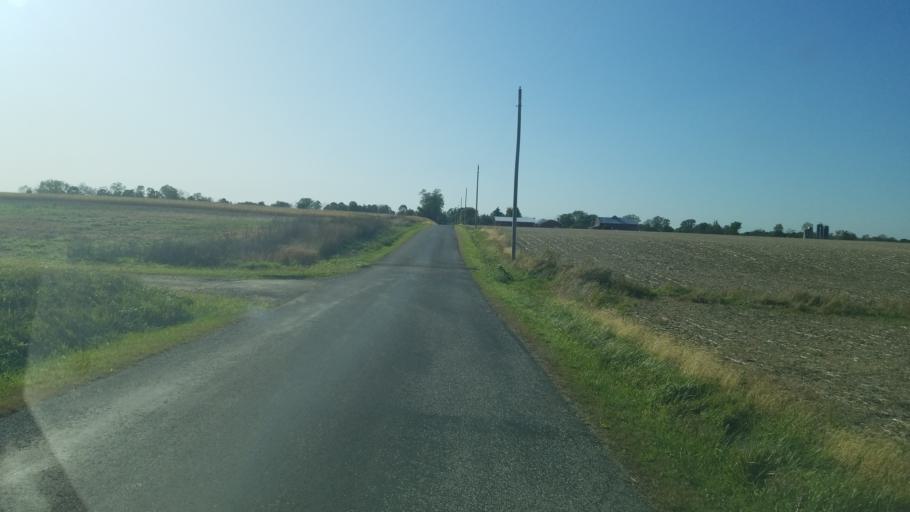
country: US
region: Ohio
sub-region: Wayne County
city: Creston
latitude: 40.9228
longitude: -81.9865
